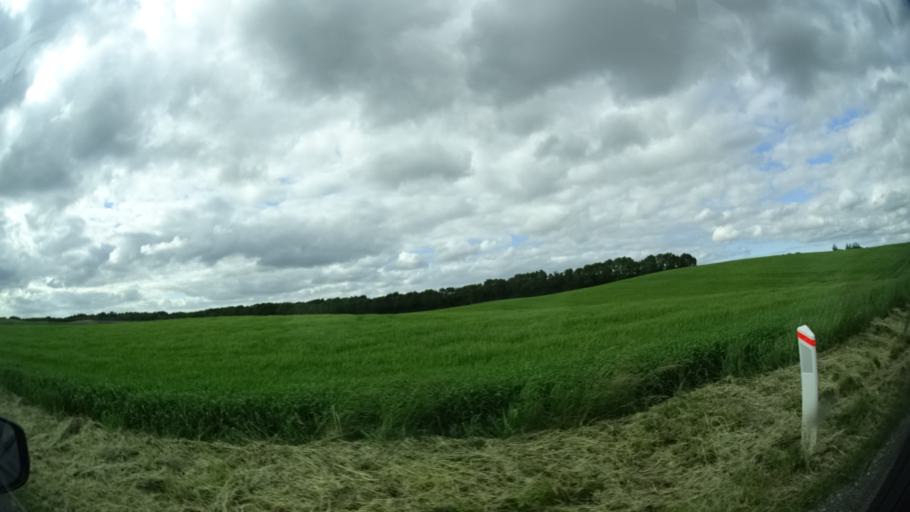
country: DK
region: Central Jutland
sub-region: Syddjurs Kommune
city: Ryomgard
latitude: 56.4055
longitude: 10.5338
